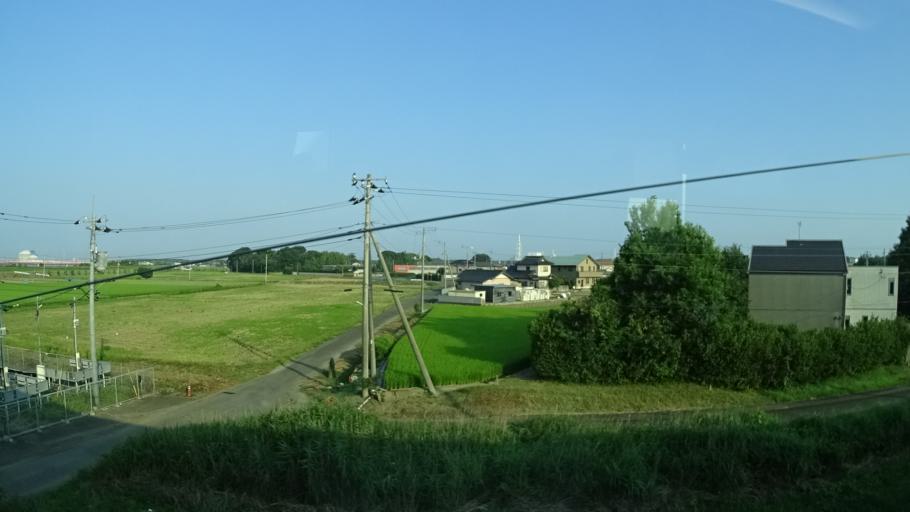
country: JP
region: Ibaraki
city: Funaishikawa
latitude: 36.4840
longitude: 140.5931
